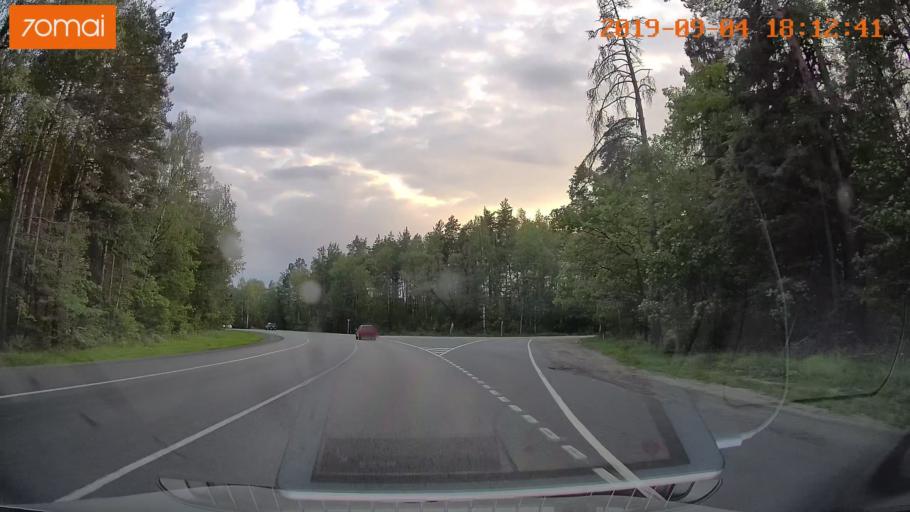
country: RU
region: Moskovskaya
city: Lopatinskiy
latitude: 55.3685
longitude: 38.7383
